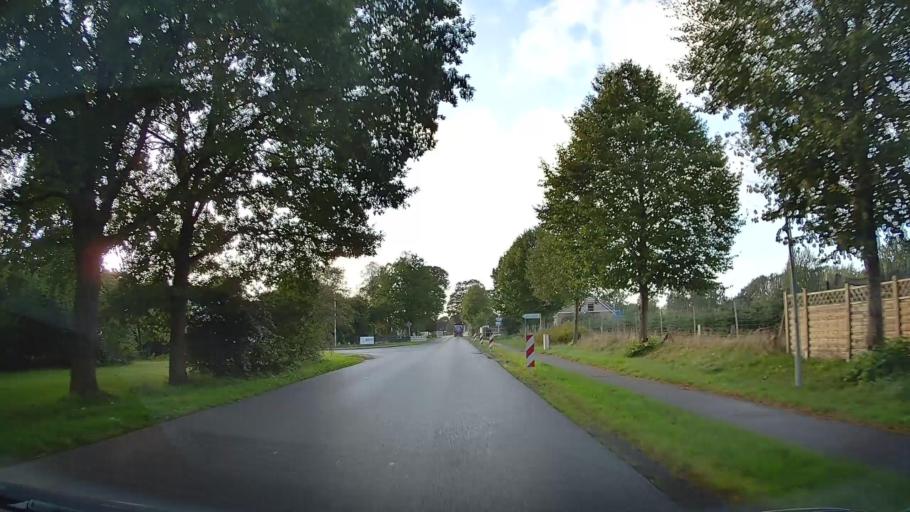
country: DE
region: Schleswig-Holstein
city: Horst
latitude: 53.8041
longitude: 9.6507
